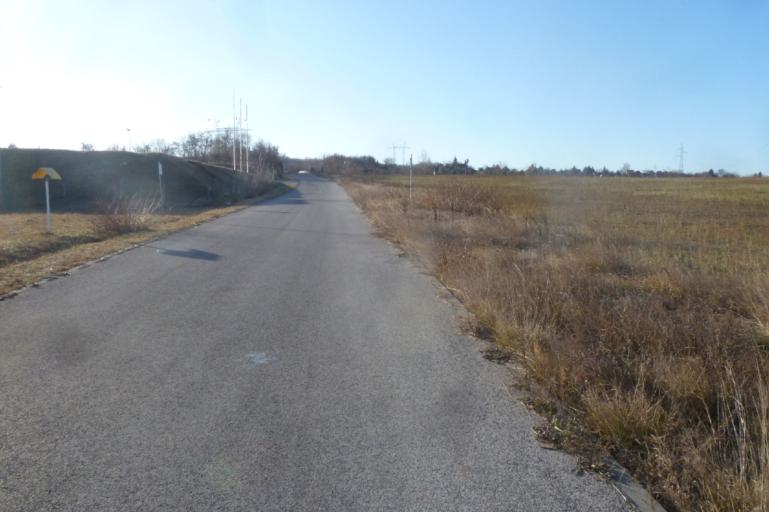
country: HU
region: Pest
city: Mogyorod
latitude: 47.5944
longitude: 19.2233
